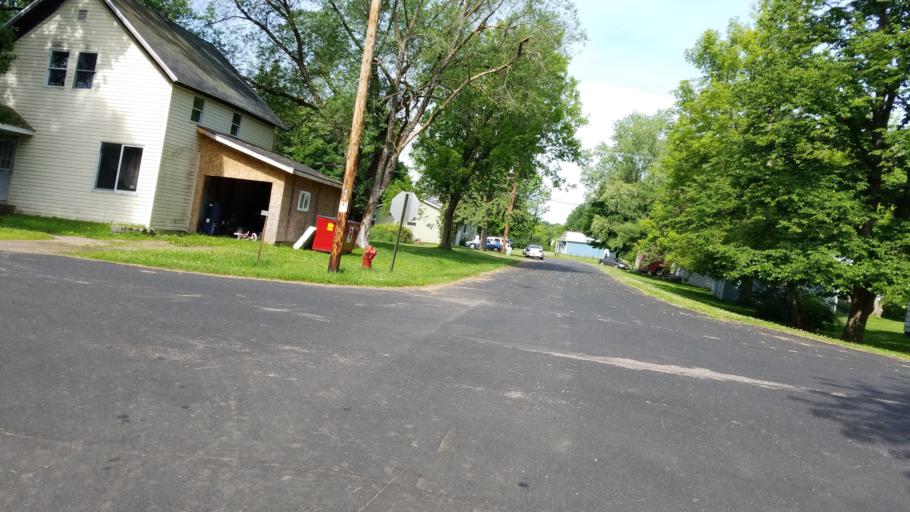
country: US
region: Wisconsin
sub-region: Dunn County
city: Menomonie
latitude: 44.7756
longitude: -91.9291
